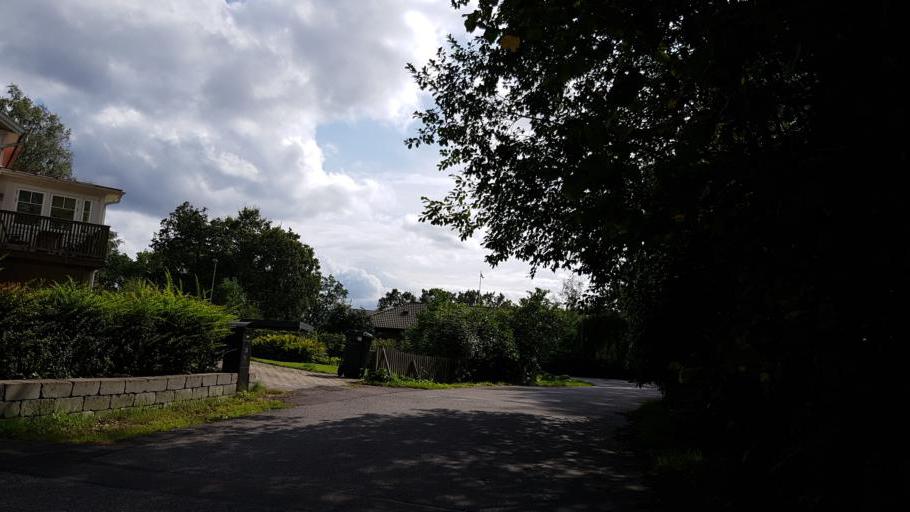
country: SE
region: Vaestra Goetaland
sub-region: Harryda Kommun
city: Molnlycke
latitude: 57.6635
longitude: 12.1074
